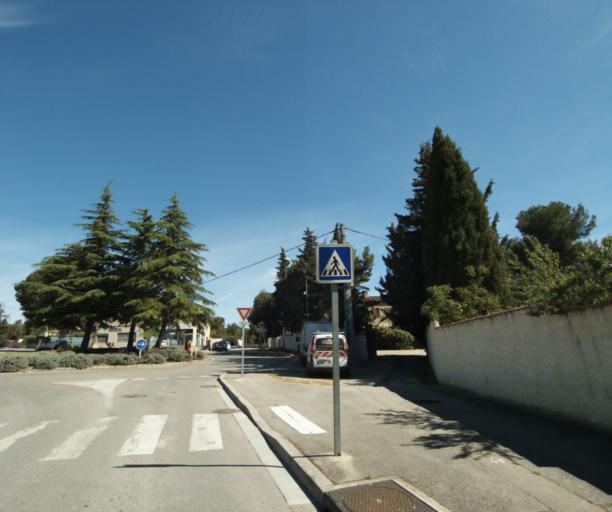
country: FR
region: Provence-Alpes-Cote d'Azur
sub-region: Departement des Bouches-du-Rhone
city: Rognac
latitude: 43.5084
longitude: 5.2186
